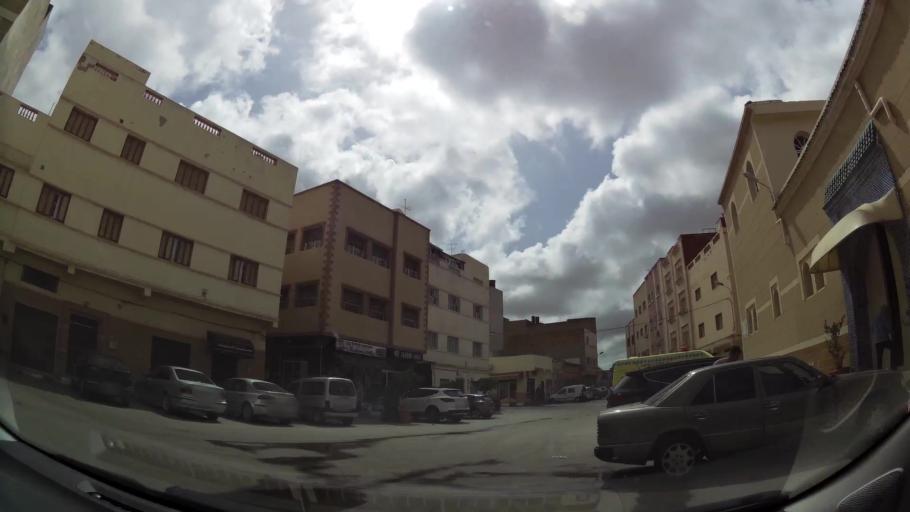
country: MA
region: Oriental
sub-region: Nador
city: Nador
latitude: 35.1721
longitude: -2.9304
